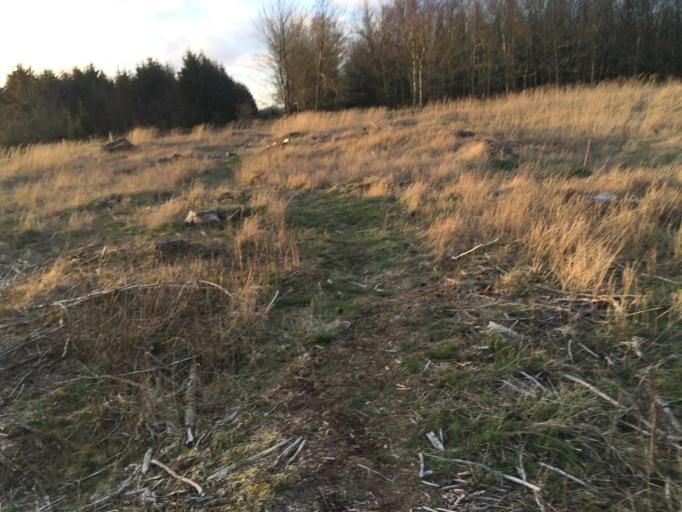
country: DK
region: Central Jutland
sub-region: Holstebro Kommune
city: Ulfborg
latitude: 56.2425
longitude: 8.4107
